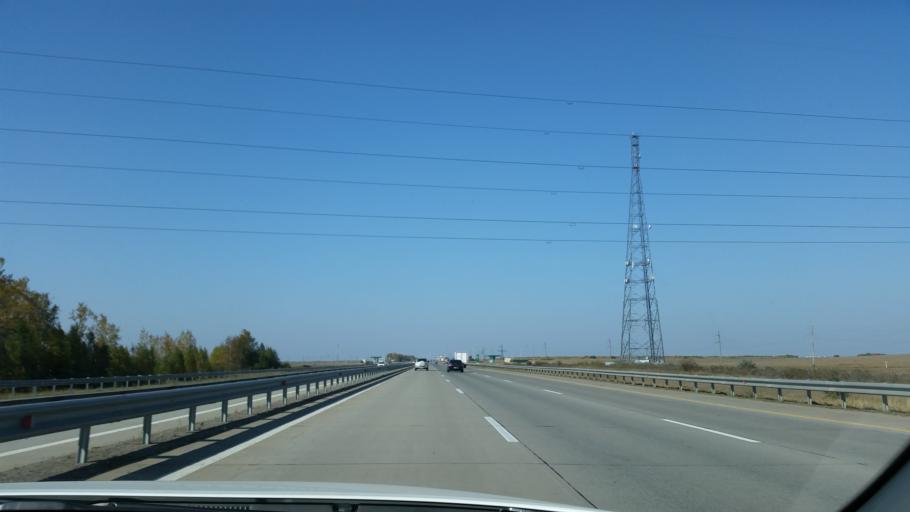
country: KZ
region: Astana Qalasy
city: Astana
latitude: 51.2948
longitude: 71.3579
